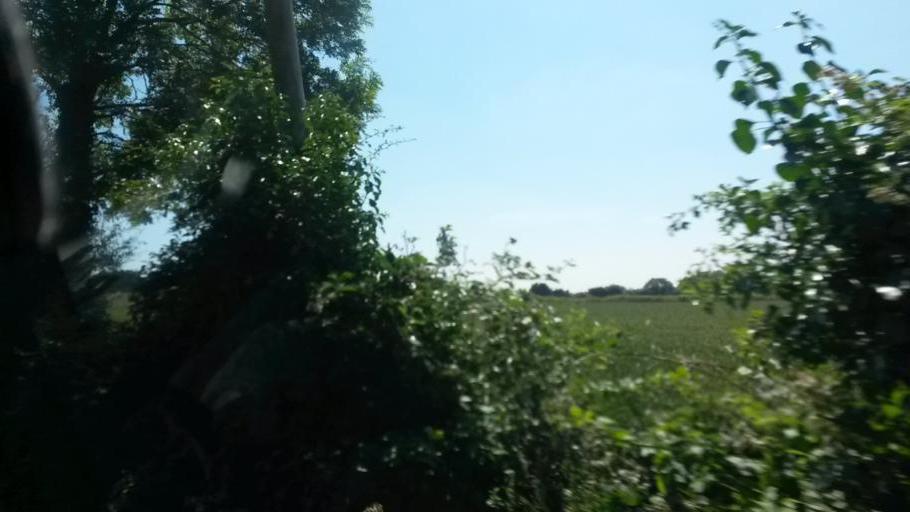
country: IE
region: Leinster
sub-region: An Mhi
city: Stamullin
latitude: 53.5639
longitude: -6.3162
